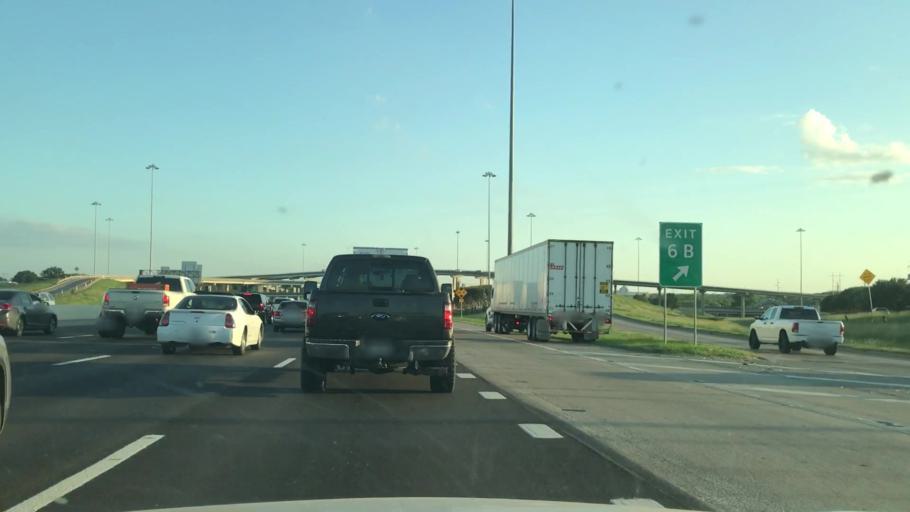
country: US
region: Texas
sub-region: Dallas County
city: Mesquite
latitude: 32.7971
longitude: -96.6260
